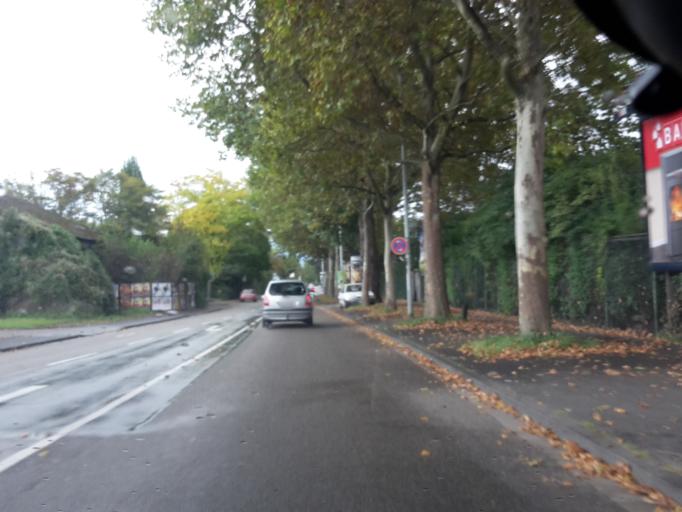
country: DE
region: Rheinland-Pfalz
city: Mainz
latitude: 49.9779
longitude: 8.2887
